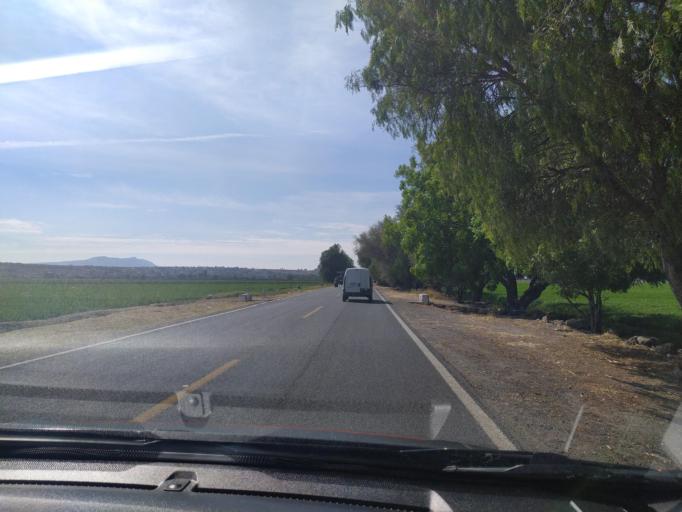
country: MX
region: Guanajuato
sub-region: San Francisco del Rincon
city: San Ignacio de Hidalgo
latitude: 20.8977
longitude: -101.8577
